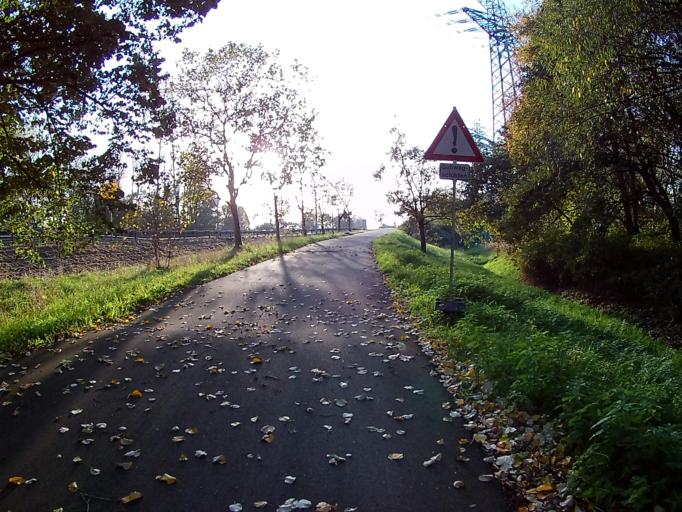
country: DE
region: Hamburg
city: Altona
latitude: 53.5157
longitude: 9.9165
